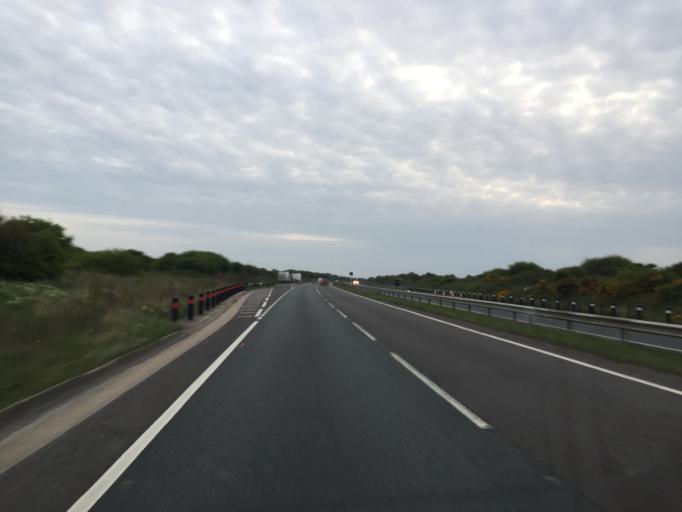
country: GB
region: England
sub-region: Kent
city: Dover
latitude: 51.1060
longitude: 1.2601
